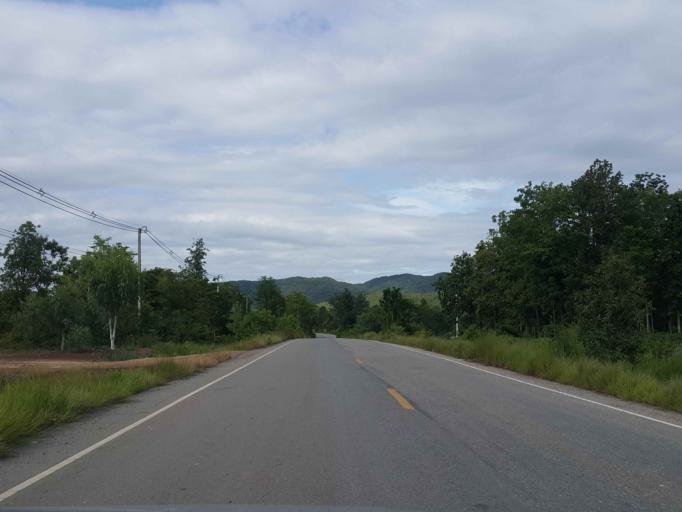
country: TH
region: Sukhothai
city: Thung Saliam
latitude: 17.2340
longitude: 99.5139
